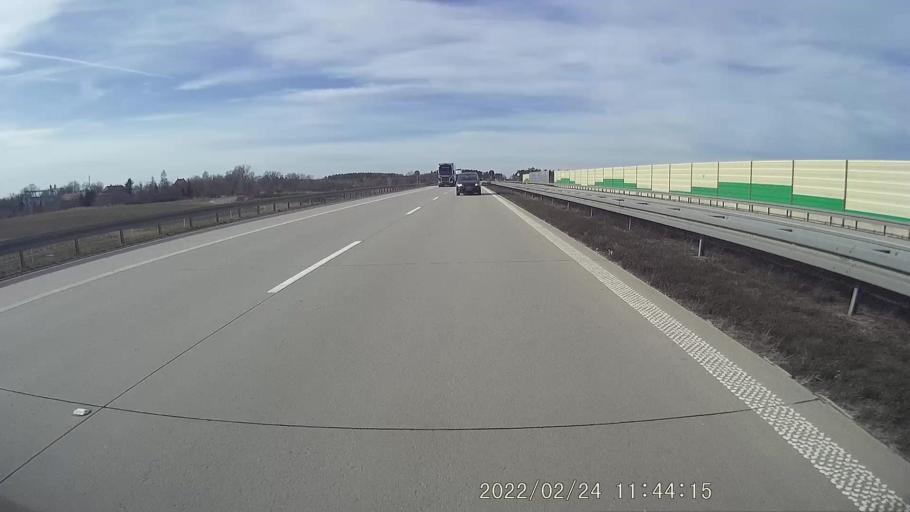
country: PL
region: Lower Silesian Voivodeship
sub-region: Powiat polkowicki
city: Radwanice
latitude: 51.5475
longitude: 15.9265
